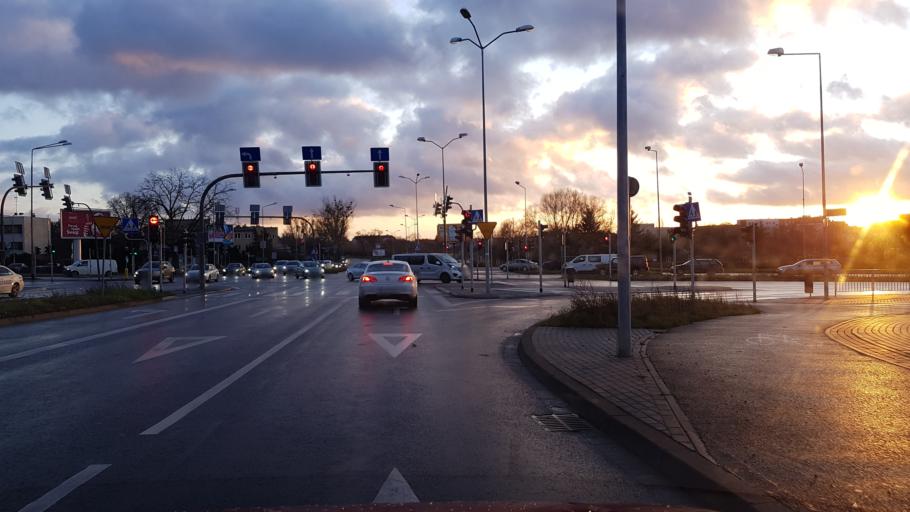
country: PL
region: West Pomeranian Voivodeship
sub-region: Szczecin
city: Szczecin
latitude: 53.4295
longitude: 14.5001
